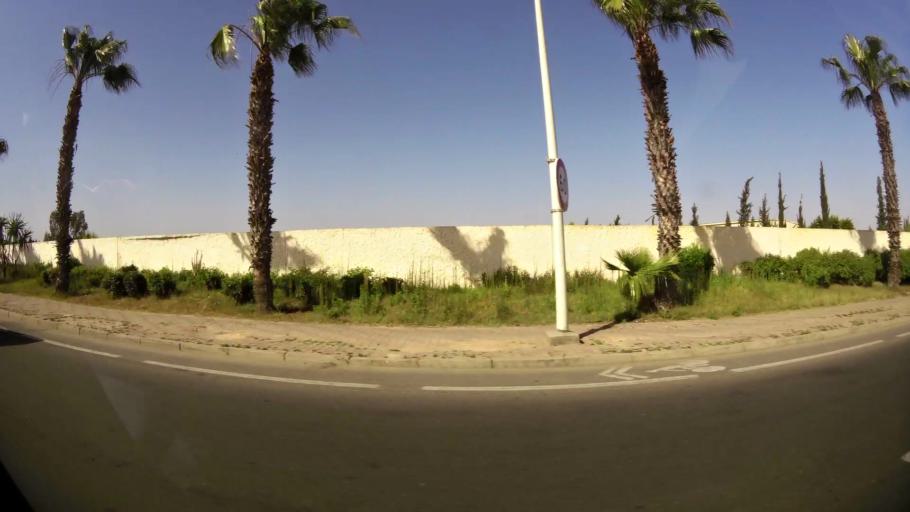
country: MA
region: Oued ed Dahab-Lagouira
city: Dakhla
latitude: 30.3804
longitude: -9.5638
